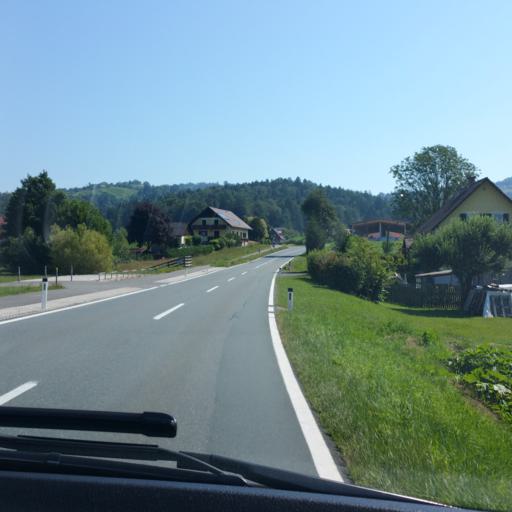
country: AT
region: Styria
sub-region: Politischer Bezirk Leibnitz
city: Gleinstatten
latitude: 46.7625
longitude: 15.3902
